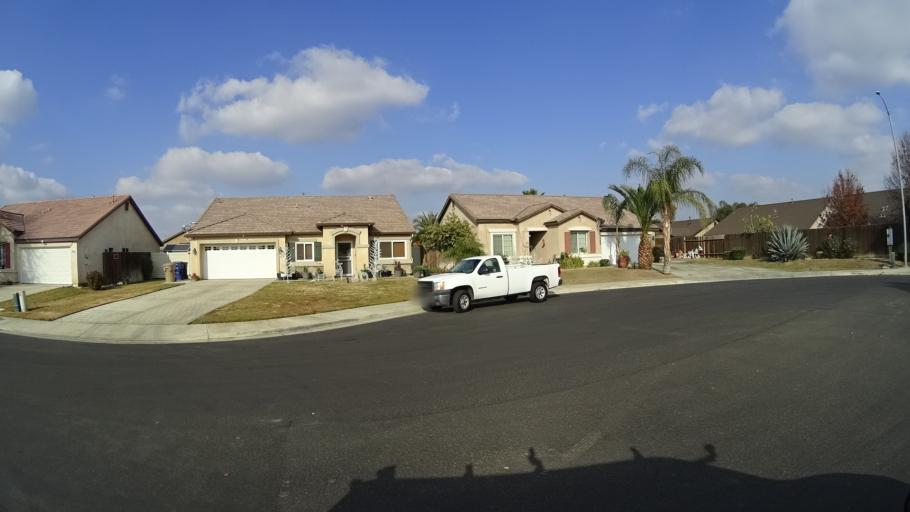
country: US
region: California
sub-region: Kern County
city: Greenacres
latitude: 35.3067
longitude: -119.1058
